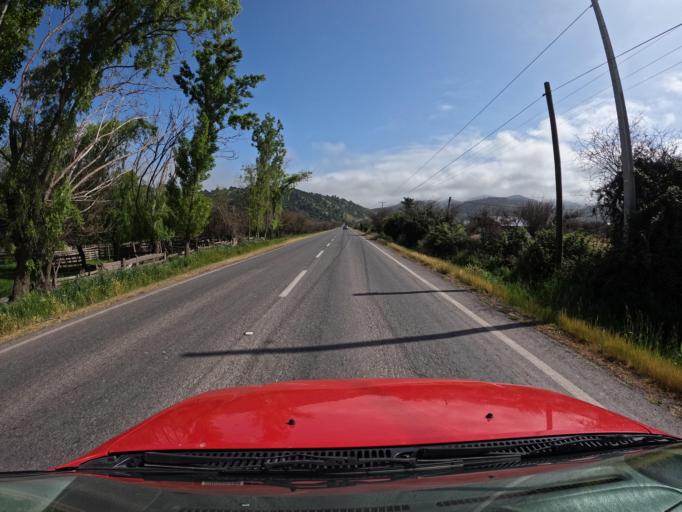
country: CL
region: Maule
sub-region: Provincia de Curico
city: Teno
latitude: -34.8305
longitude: -71.1903
